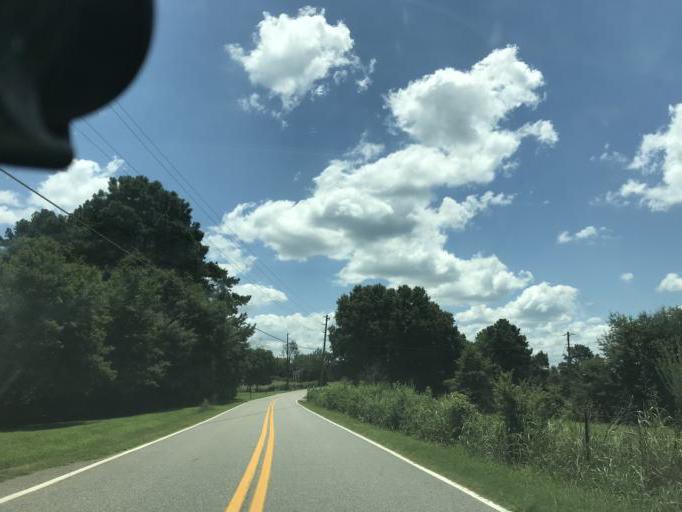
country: US
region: Georgia
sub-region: Fulton County
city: Milton
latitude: 34.2320
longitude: -84.2574
